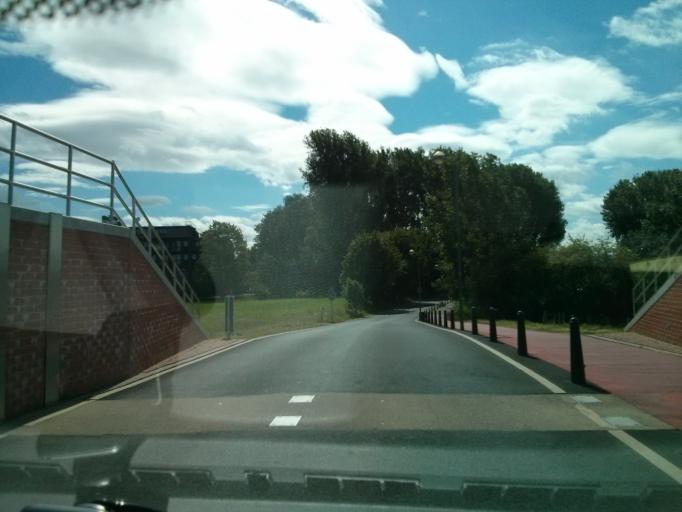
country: DE
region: North Rhine-Westphalia
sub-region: Regierungsbezirk Dusseldorf
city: Meerbusch
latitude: 51.2993
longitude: 6.7201
